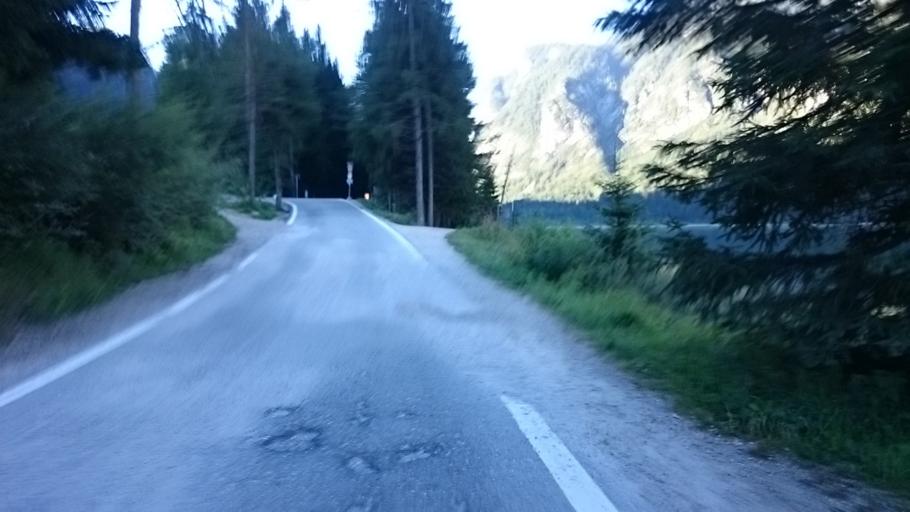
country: IT
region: Trentino-Alto Adige
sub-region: Bolzano
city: Dobbiaco
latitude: 46.7055
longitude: 12.2198
